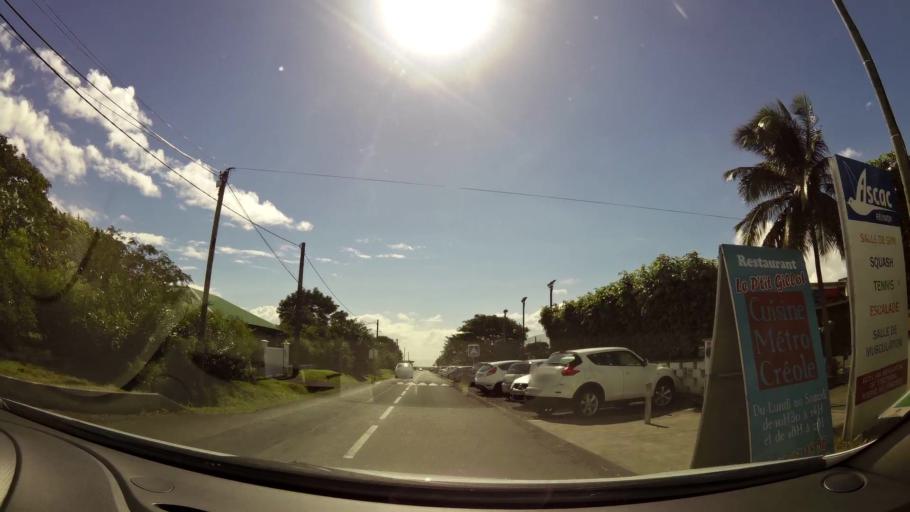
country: RE
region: Reunion
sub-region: Reunion
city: Sainte-Marie
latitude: -20.8932
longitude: 55.5094
